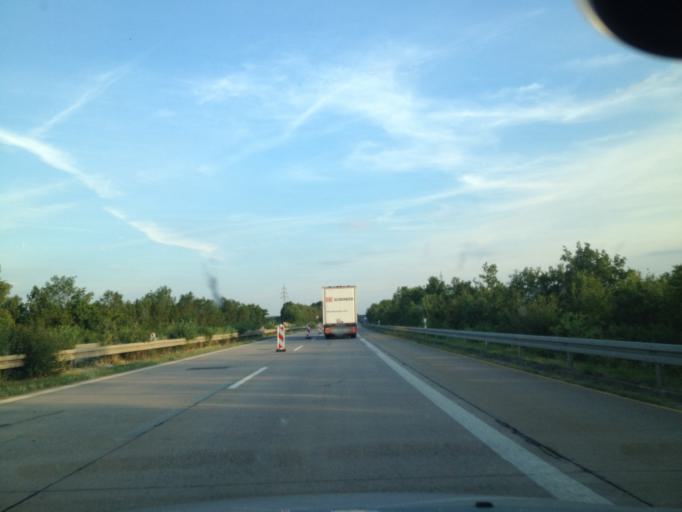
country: DE
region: Bavaria
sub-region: Regierungsbezirk Unterfranken
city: Biebelried
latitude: 49.7462
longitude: 10.1072
